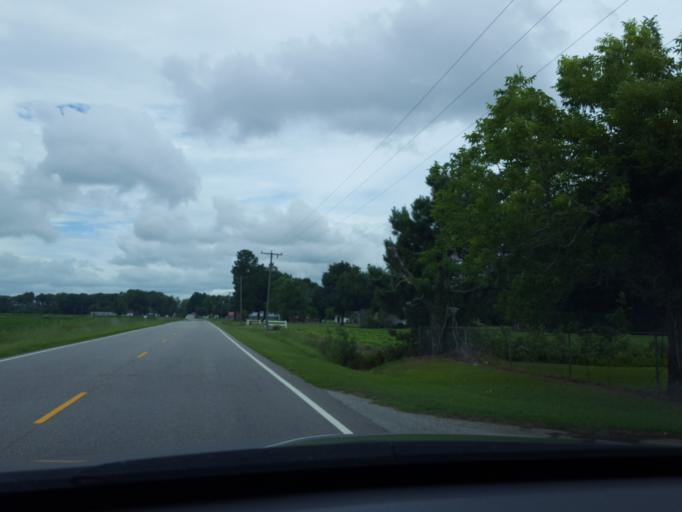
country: US
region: North Carolina
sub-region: Martin County
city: Williamston
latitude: 35.7296
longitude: -76.9791
